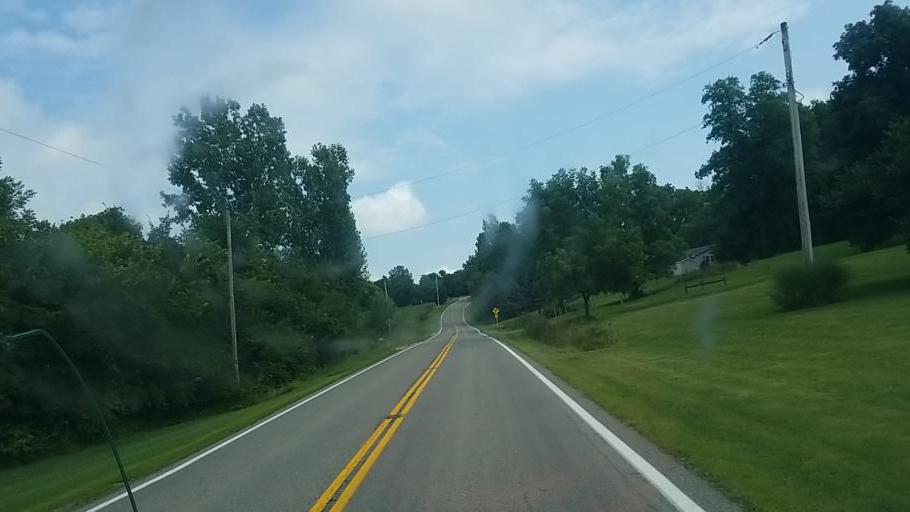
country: US
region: Ohio
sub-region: Champaign County
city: North Lewisburg
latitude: 40.2591
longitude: -83.6366
